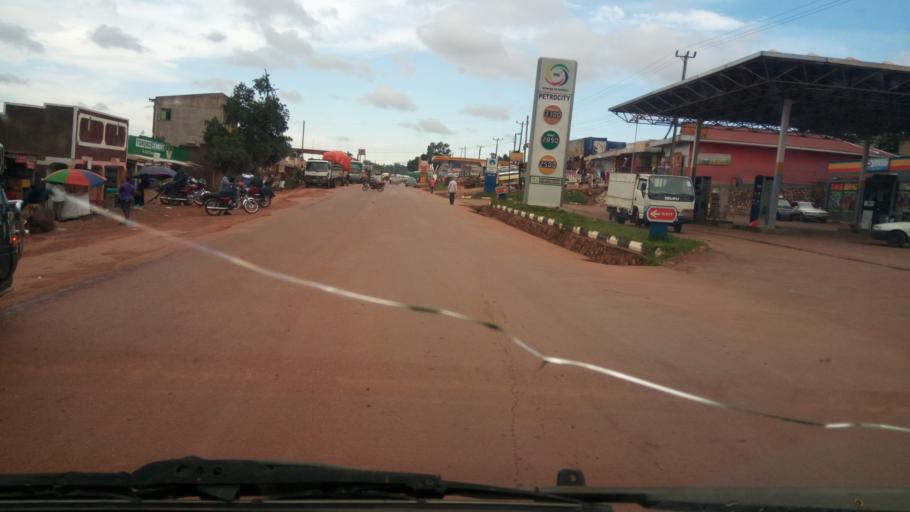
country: UG
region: Central Region
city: Kampala Central Division
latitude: 0.3328
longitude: 32.5515
